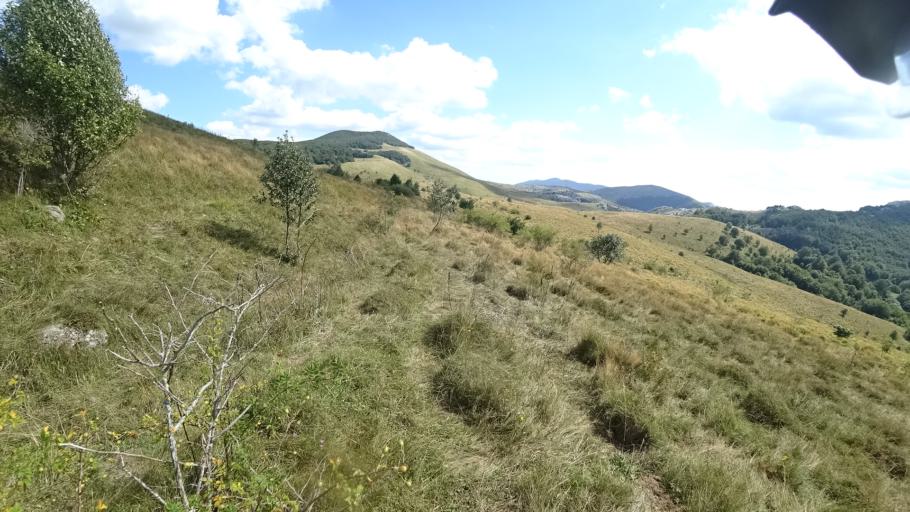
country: HR
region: Zadarska
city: Gracac
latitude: 44.4205
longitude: 15.9978
